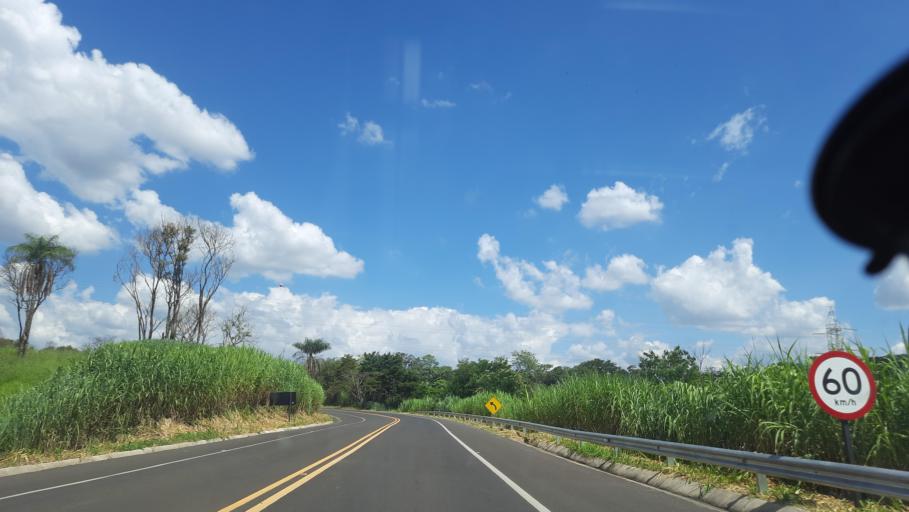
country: BR
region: Sao Paulo
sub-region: Sao Jose Do Rio Pardo
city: Sao Jose do Rio Pardo
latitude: -21.6061
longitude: -46.9671
